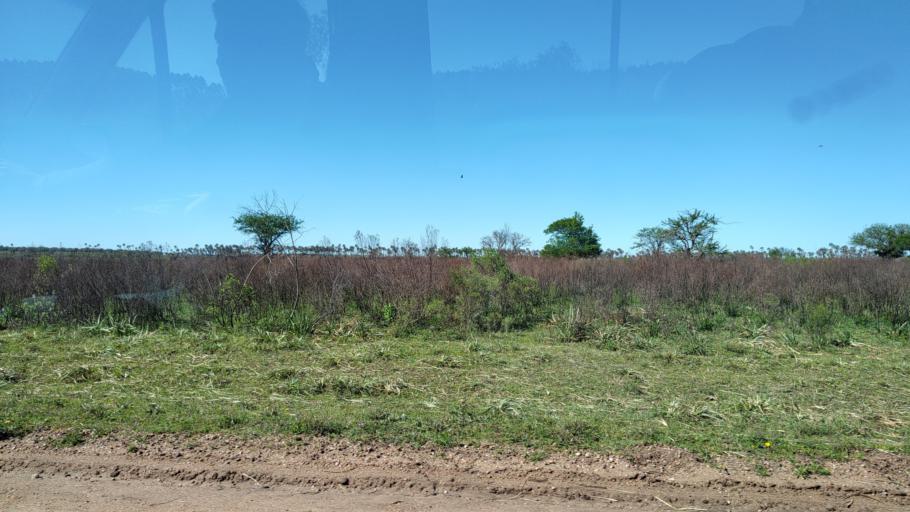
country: AR
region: Entre Rios
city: Ubajay
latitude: -31.8634
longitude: -58.2694
